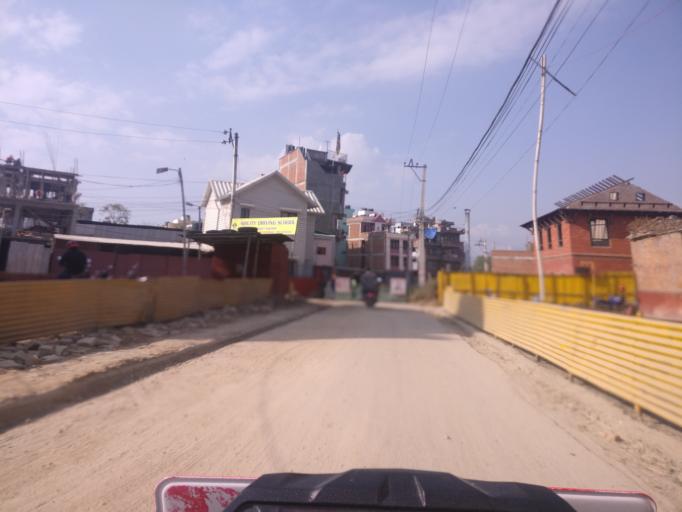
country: NP
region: Central Region
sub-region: Bagmati Zone
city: Patan
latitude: 27.6813
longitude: 85.3290
